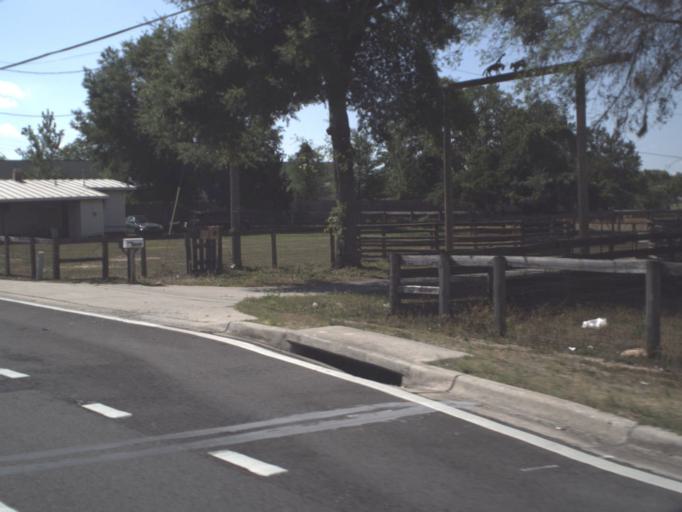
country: US
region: Florida
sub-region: Marion County
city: Ocala
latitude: 29.1867
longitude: -82.2047
